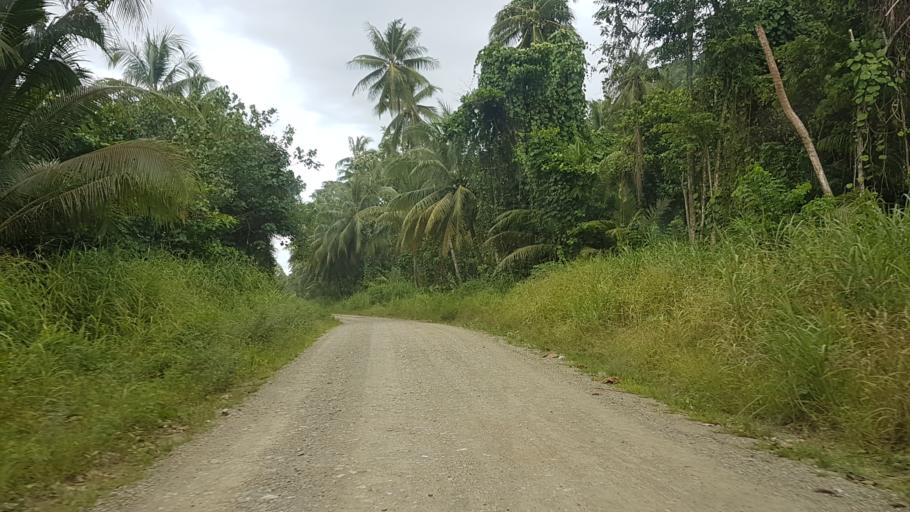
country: PG
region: East Sepik
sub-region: Wewak
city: Wewak
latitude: -3.4106
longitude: 143.3489
